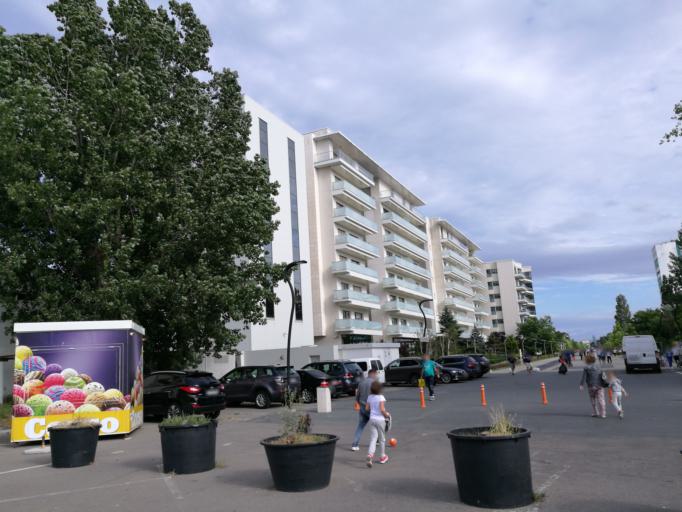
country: RO
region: Constanta
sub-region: Municipiul Constanta
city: Palazu Mare
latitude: 44.2476
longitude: 28.6221
